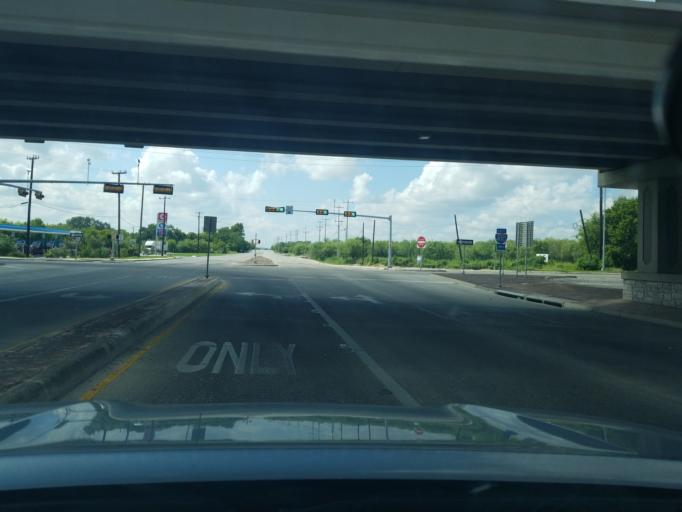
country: US
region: Texas
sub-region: Bexar County
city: Lackland Air Force Base
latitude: 29.3202
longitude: -98.5326
